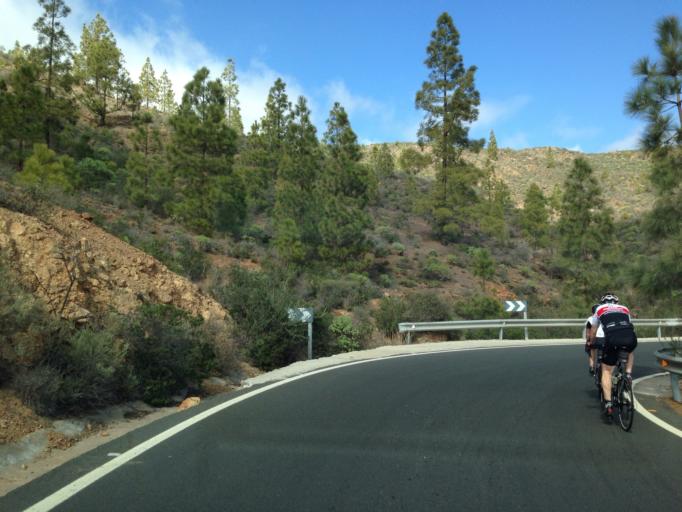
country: ES
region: Canary Islands
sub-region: Provincia de Las Palmas
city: San Bartolome
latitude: 27.9026
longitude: -15.5692
